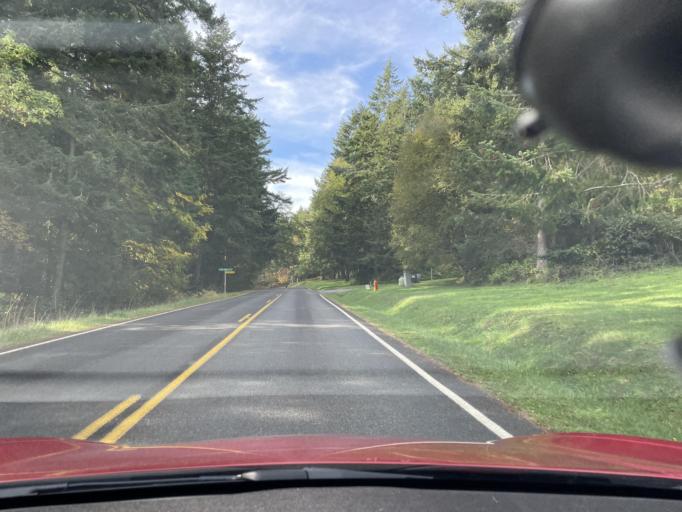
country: US
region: Washington
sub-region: San Juan County
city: Friday Harbor
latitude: 48.5290
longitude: -122.9873
